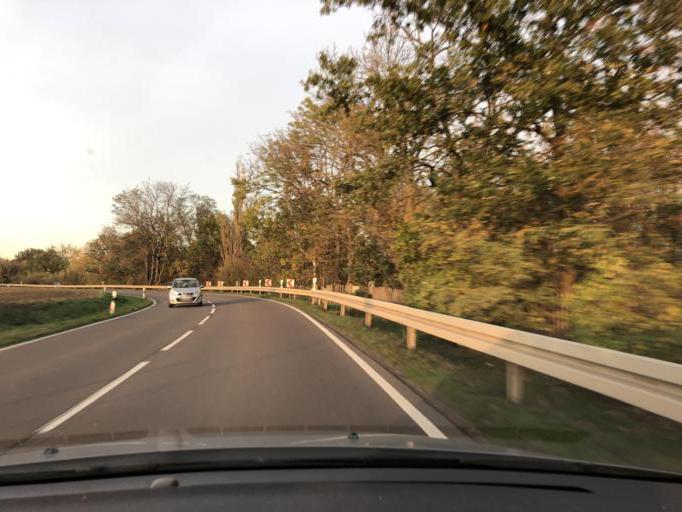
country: DE
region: Saxony-Anhalt
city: Zeitz
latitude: 51.0929
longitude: 12.1758
